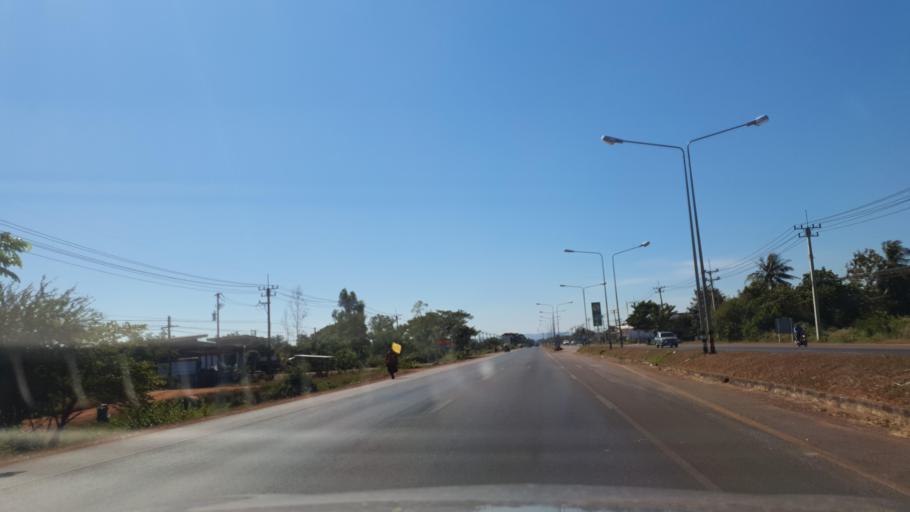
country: TH
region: Sakon Nakhon
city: Sakon Nakhon
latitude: 17.2484
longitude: 104.1128
